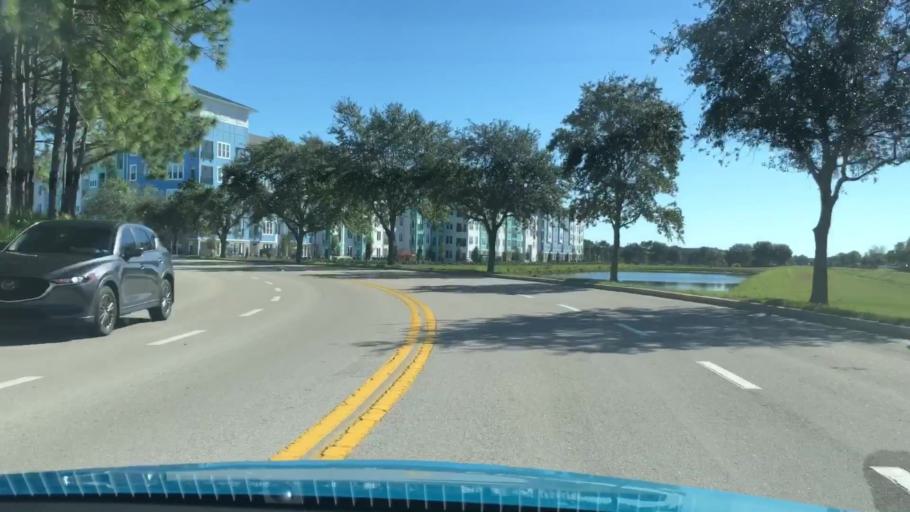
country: US
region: Florida
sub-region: Orange County
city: Oak Ridge
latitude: 28.4832
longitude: -81.4330
